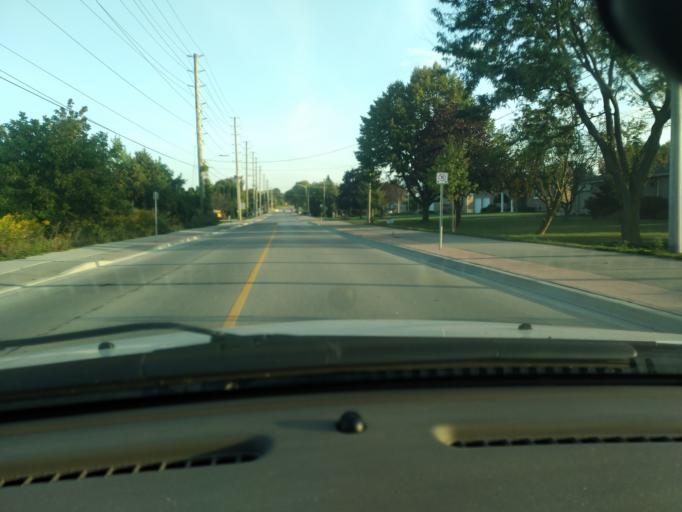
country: CA
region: Ontario
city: Bradford West Gwillimbury
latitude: 44.0969
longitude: -79.5681
